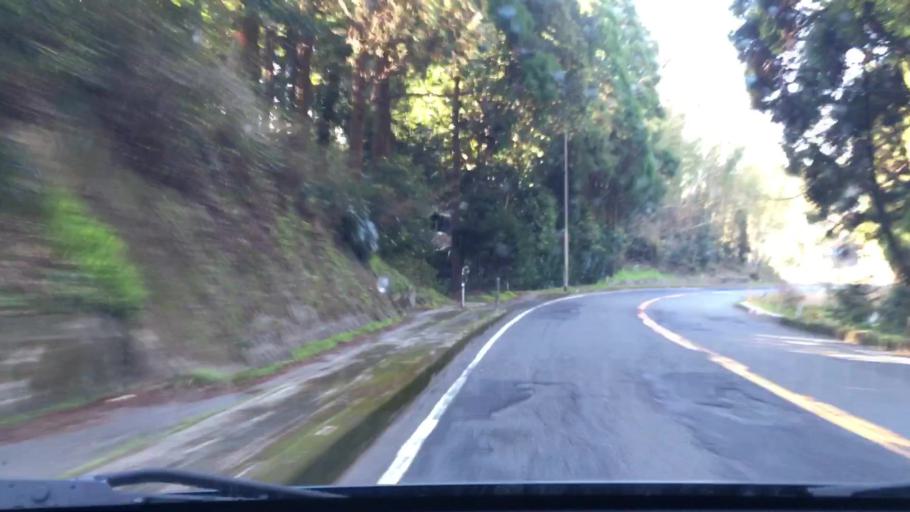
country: JP
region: Kagoshima
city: Sueyoshicho-ninokata
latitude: 31.6731
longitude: 130.9244
